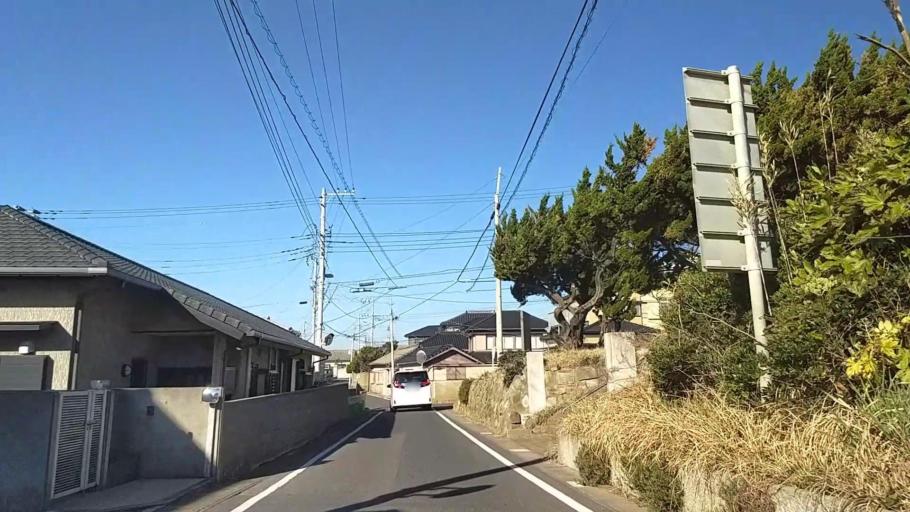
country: JP
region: Chiba
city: Hasaki
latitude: 35.6957
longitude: 140.8571
